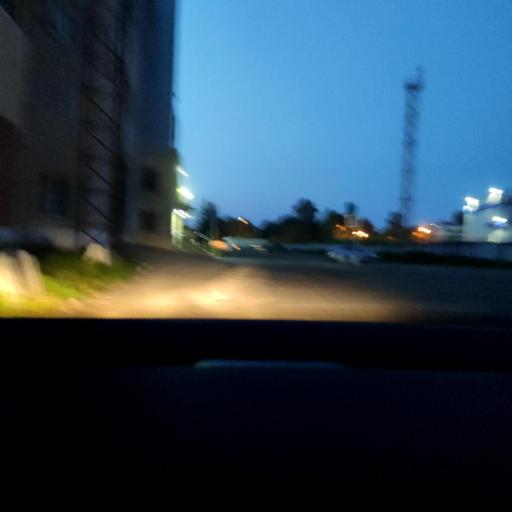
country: RU
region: Moskovskaya
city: Zheleznodorozhnyy
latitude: 55.7287
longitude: 38.0124
